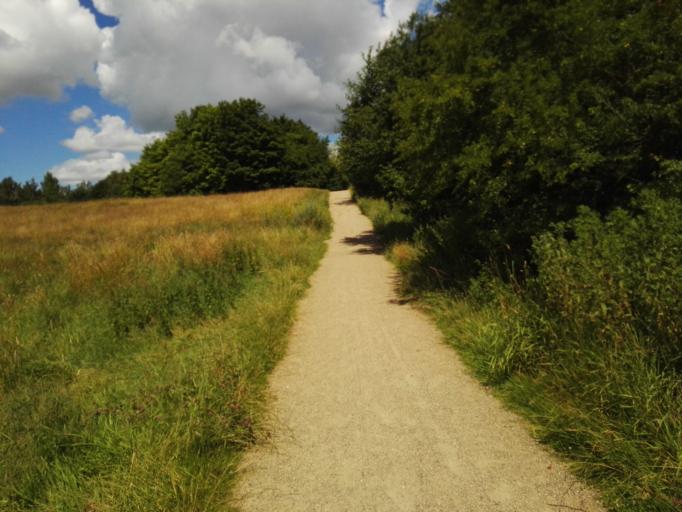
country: DK
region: Capital Region
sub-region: Ballerup Kommune
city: Ballerup
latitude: 55.7430
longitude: 12.3605
